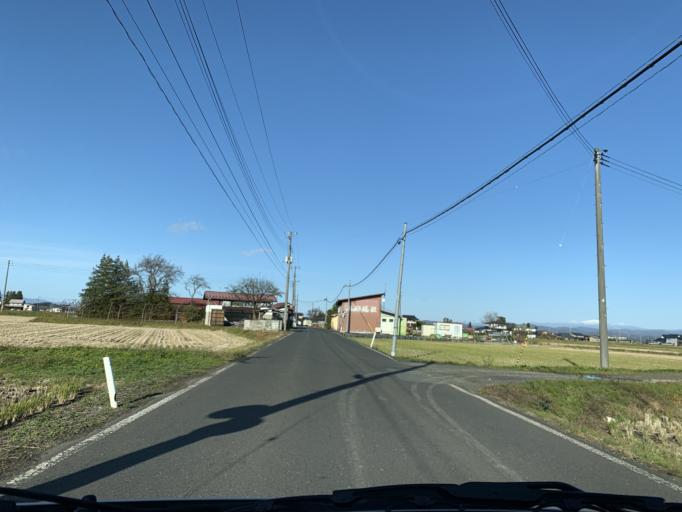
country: JP
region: Iwate
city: Mizusawa
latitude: 39.1562
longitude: 141.0974
